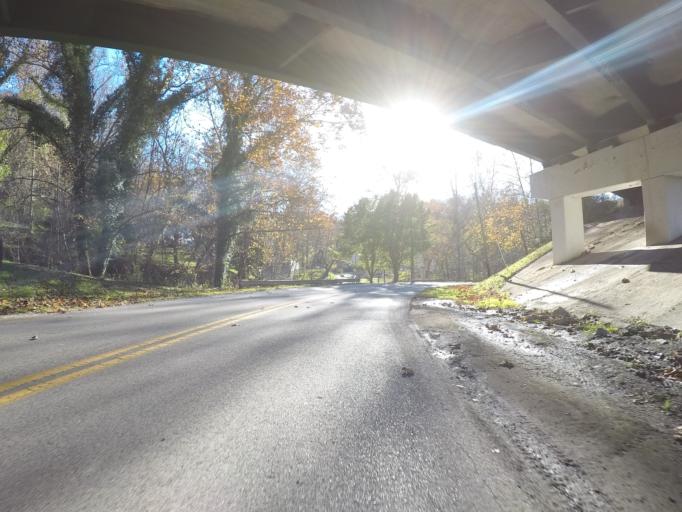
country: US
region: West Virginia
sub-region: Wayne County
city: Ceredo
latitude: 38.3903
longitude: -82.5650
